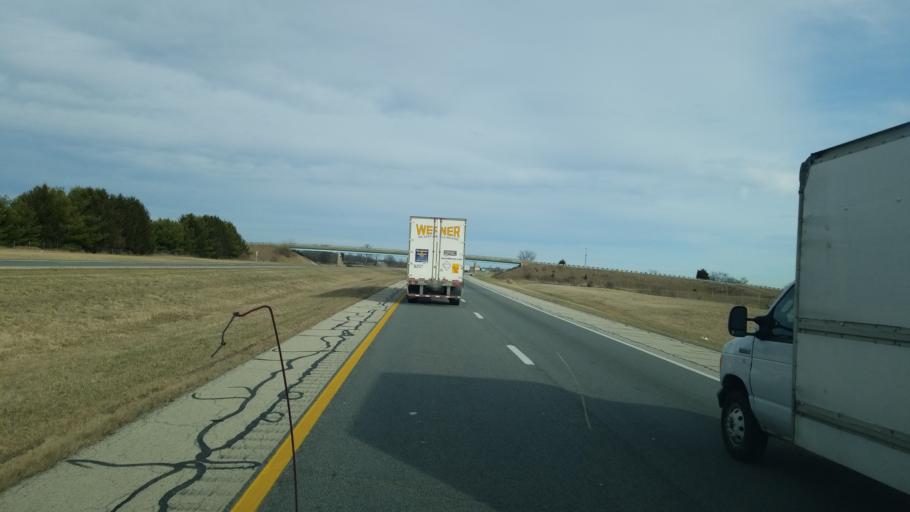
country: US
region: Ohio
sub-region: Madison County
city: Bethel
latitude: 39.7246
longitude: -83.3930
